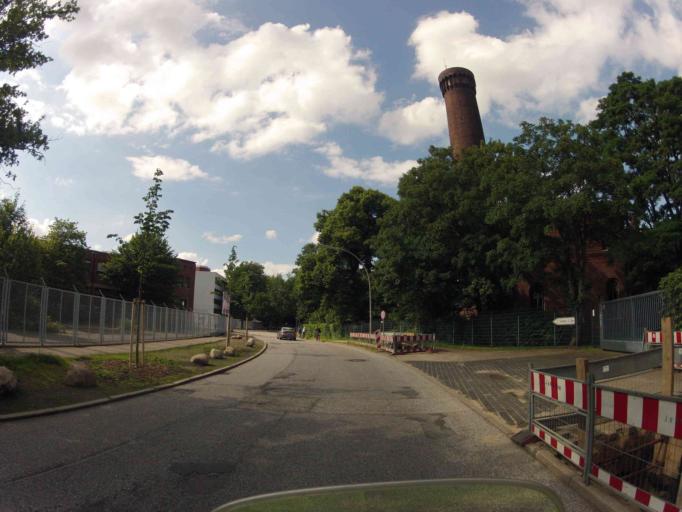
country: DE
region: Hamburg
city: Rothenburgsort
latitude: 53.5313
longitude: 10.0418
